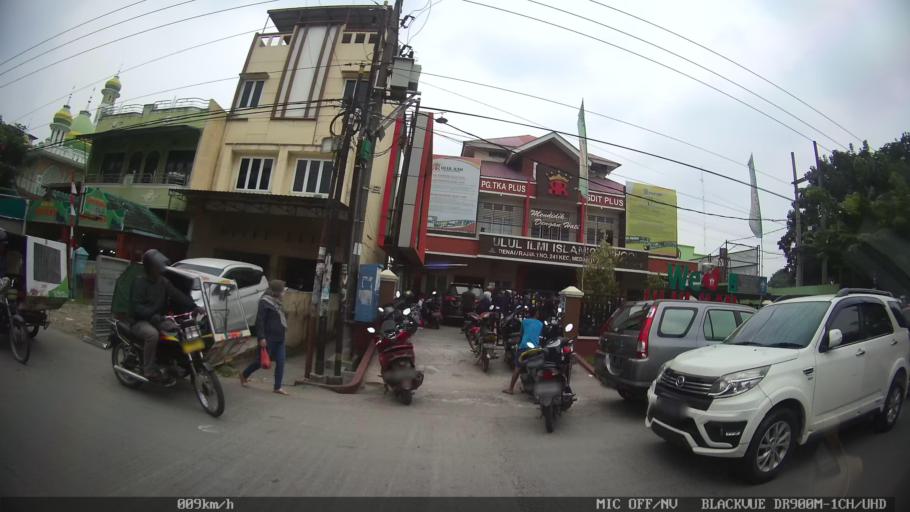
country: ID
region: North Sumatra
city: Medan
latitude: 3.5815
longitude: 98.7230
